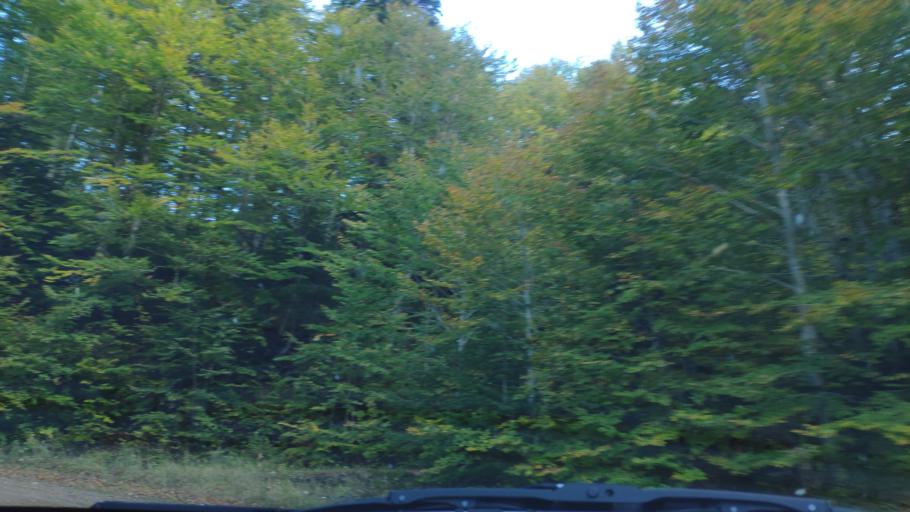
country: GR
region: West Macedonia
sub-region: Nomos Kastorias
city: Nestorio
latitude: 40.3298
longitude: 20.9018
